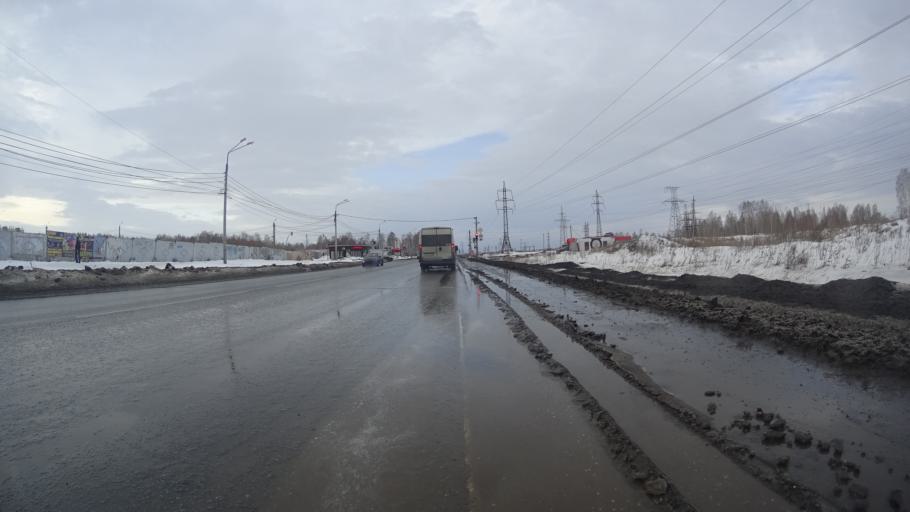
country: RU
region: Chelyabinsk
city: Roshchino
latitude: 55.2200
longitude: 61.2977
